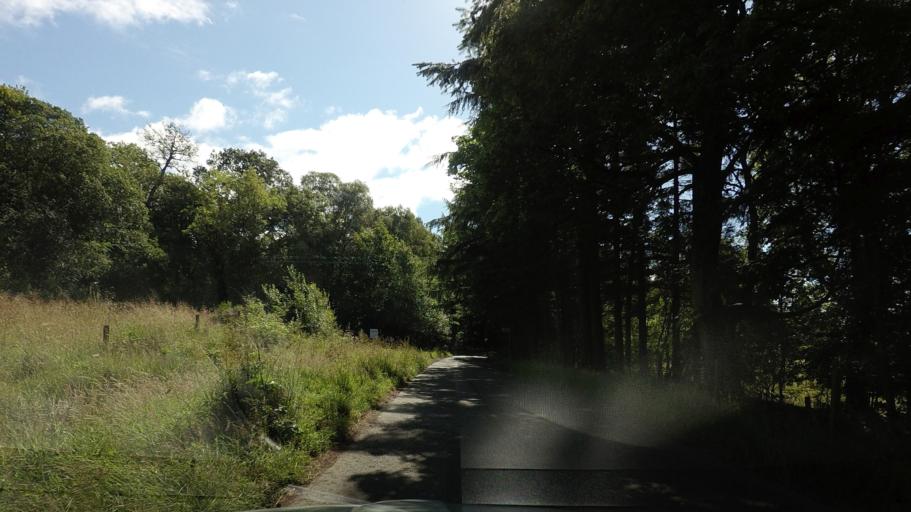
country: GB
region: Scotland
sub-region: Stirling
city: Killearn
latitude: 56.0625
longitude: -4.4619
